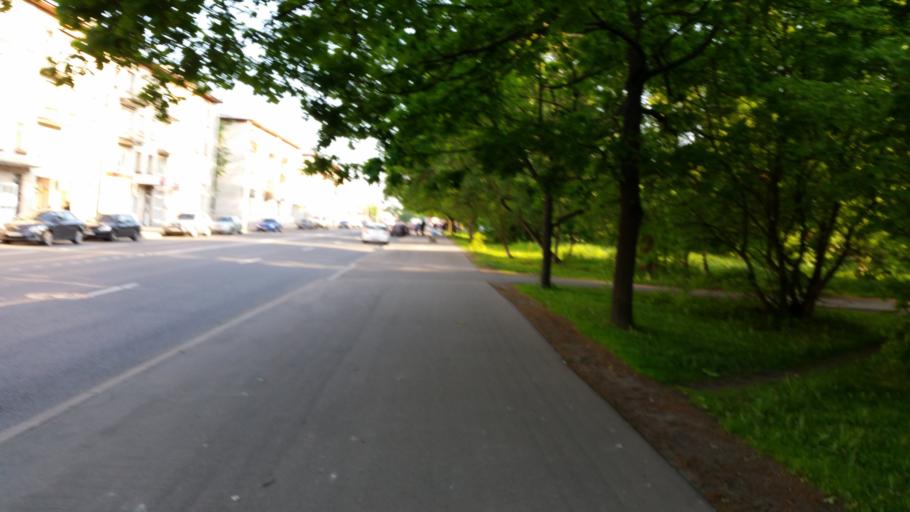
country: RU
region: St.-Petersburg
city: Sosnovaya Polyana
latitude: 59.8385
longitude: 30.1466
